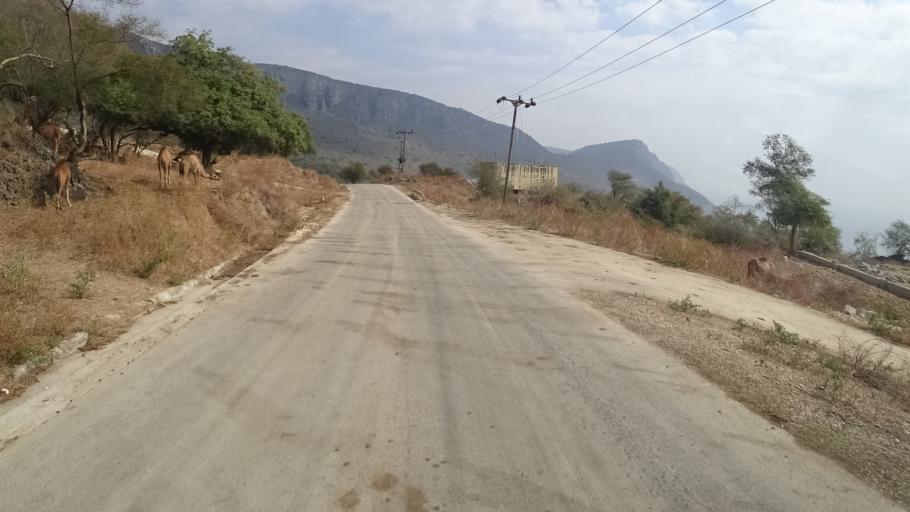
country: YE
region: Al Mahrah
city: Hawf
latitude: 16.7110
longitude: 53.2470
